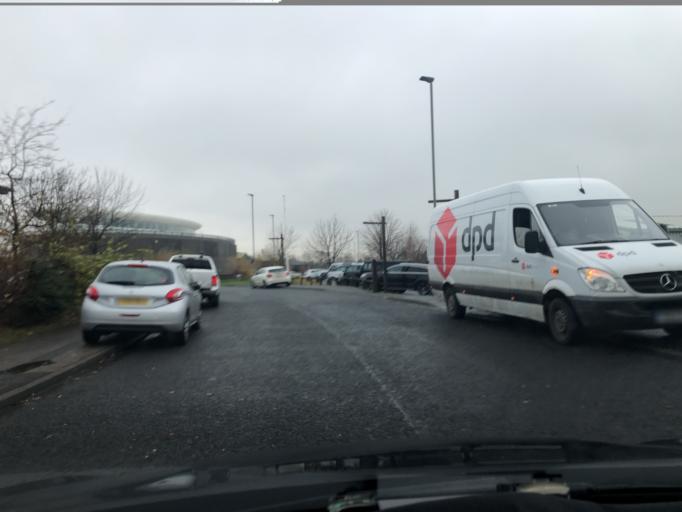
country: GB
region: England
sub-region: North Yorkshire
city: Stokesley
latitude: 54.4613
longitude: -1.1772
